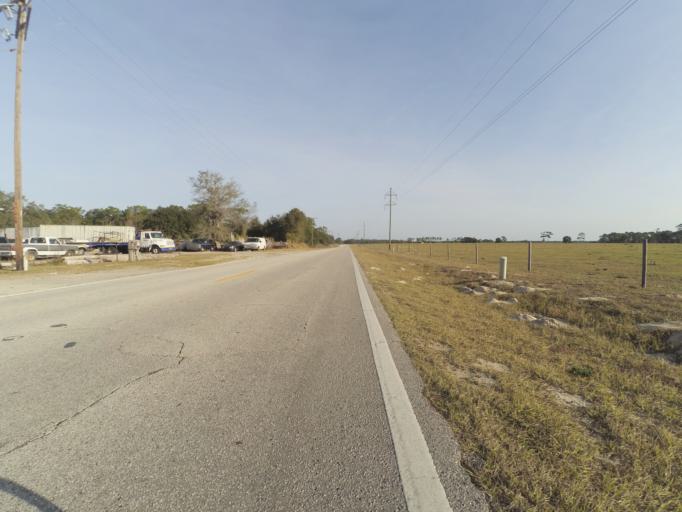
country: US
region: Florida
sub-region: Lake County
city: Umatilla
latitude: 28.9544
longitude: -81.6297
